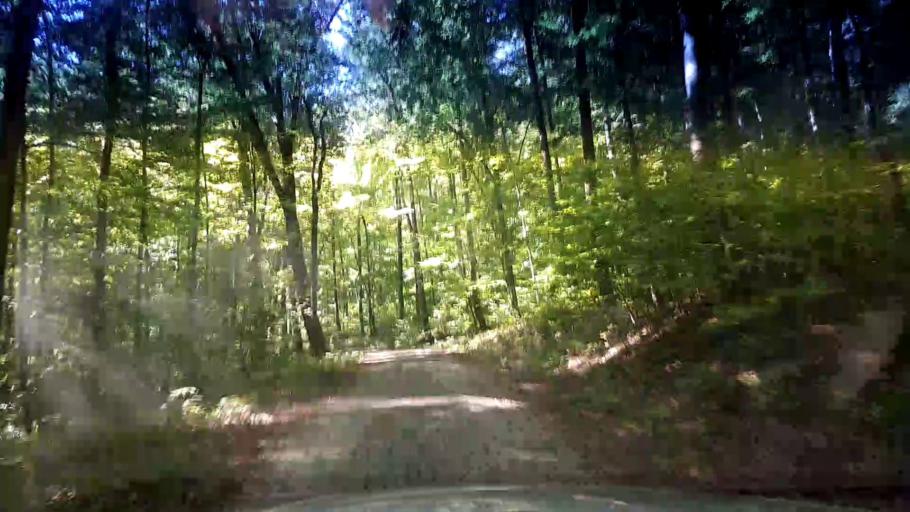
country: DE
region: Bavaria
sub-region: Upper Franconia
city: Litzendorf
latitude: 49.8841
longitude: 11.0553
